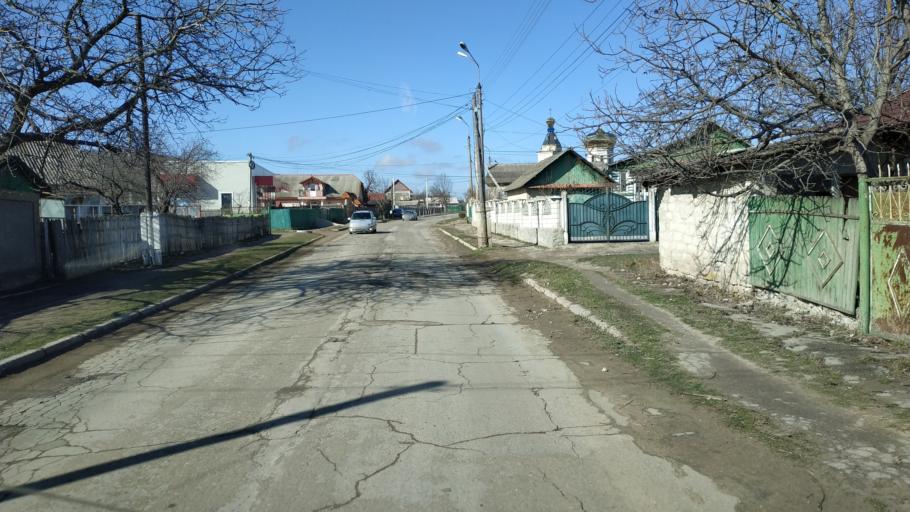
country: MD
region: Hincesti
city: Hincesti
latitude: 46.9718
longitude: 28.5832
